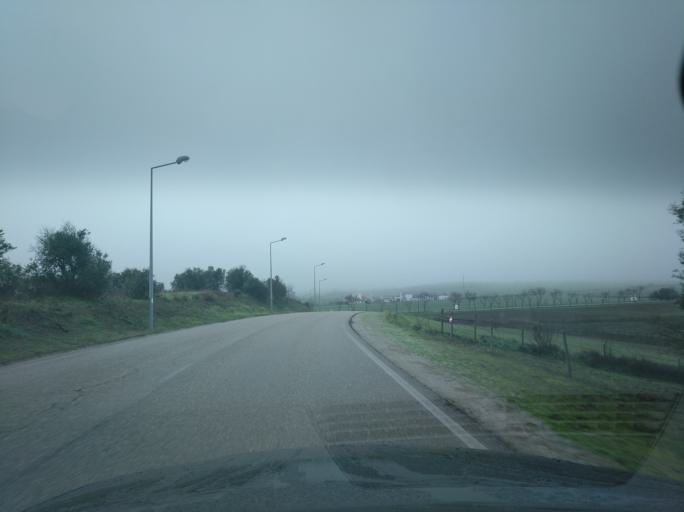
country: PT
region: Portalegre
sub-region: Campo Maior
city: Campo Maior
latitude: 39.0229
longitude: -7.0759
